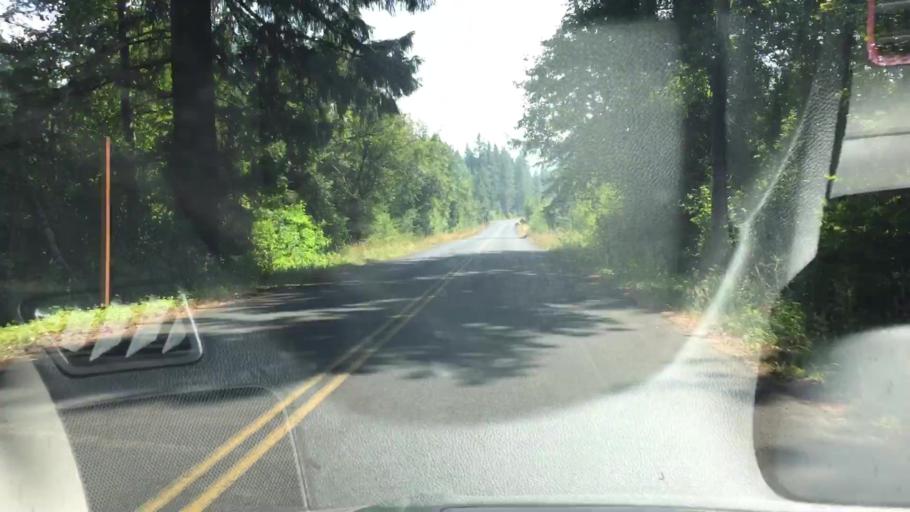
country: US
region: Washington
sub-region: Klickitat County
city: White Salmon
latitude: 46.0172
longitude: -121.5288
